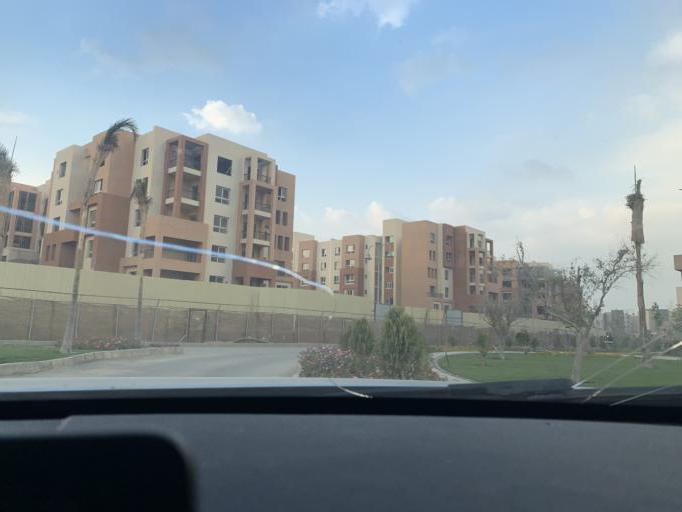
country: EG
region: Muhafazat al Qalyubiyah
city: Al Khankah
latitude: 30.0978
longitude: 31.6513
